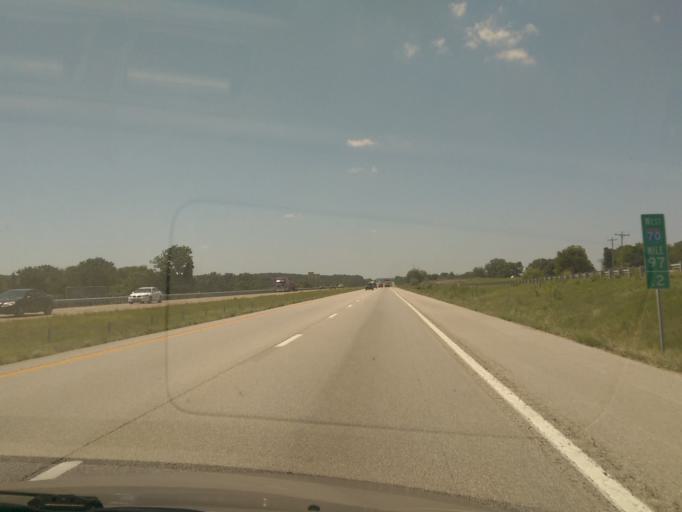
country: US
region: Missouri
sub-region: Cooper County
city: Boonville
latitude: 38.9353
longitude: -92.8623
